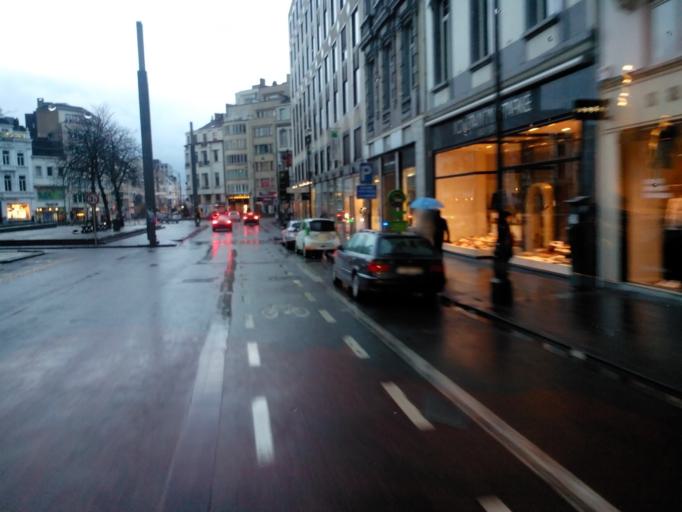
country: BE
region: Brussels Capital
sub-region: Bruxelles-Capitale
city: Brussels
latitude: 50.8328
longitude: 4.3585
